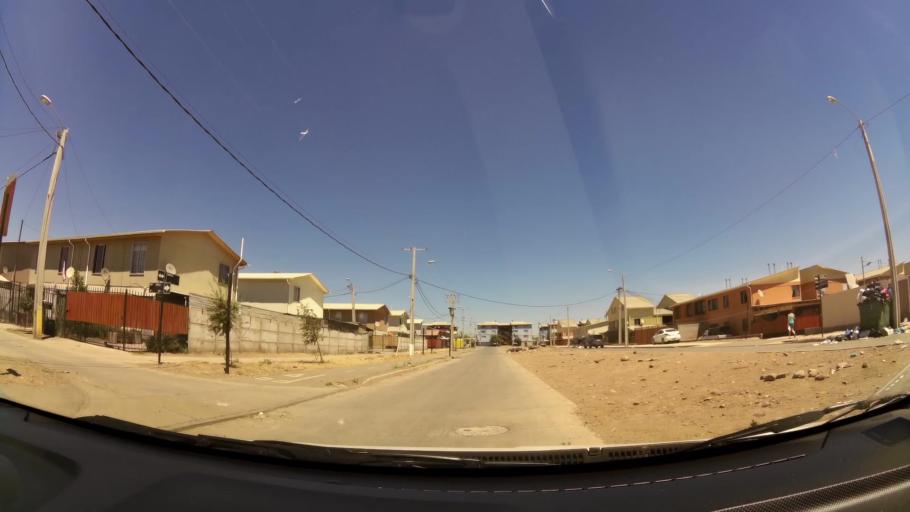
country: CL
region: O'Higgins
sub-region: Provincia de Cachapoal
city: Machali
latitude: -34.1597
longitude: -70.6949
